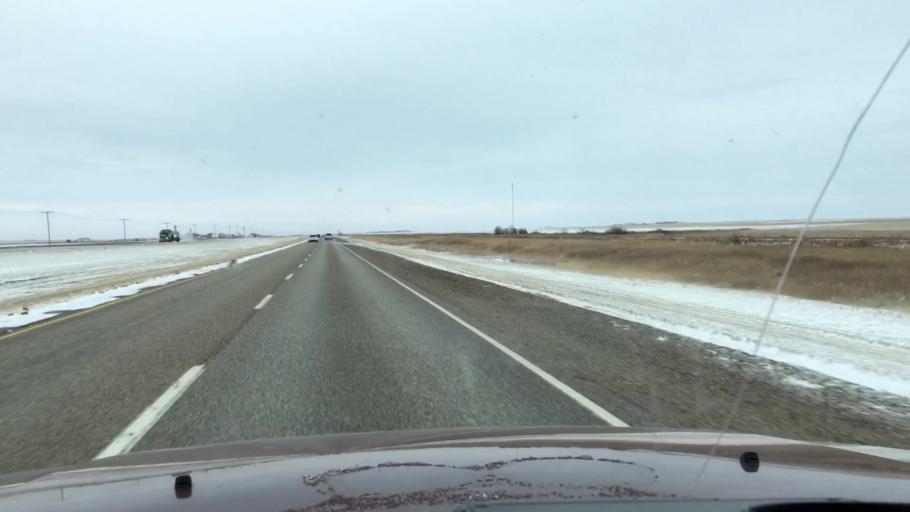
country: CA
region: Saskatchewan
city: Moose Jaw
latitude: 51.0216
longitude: -105.7879
